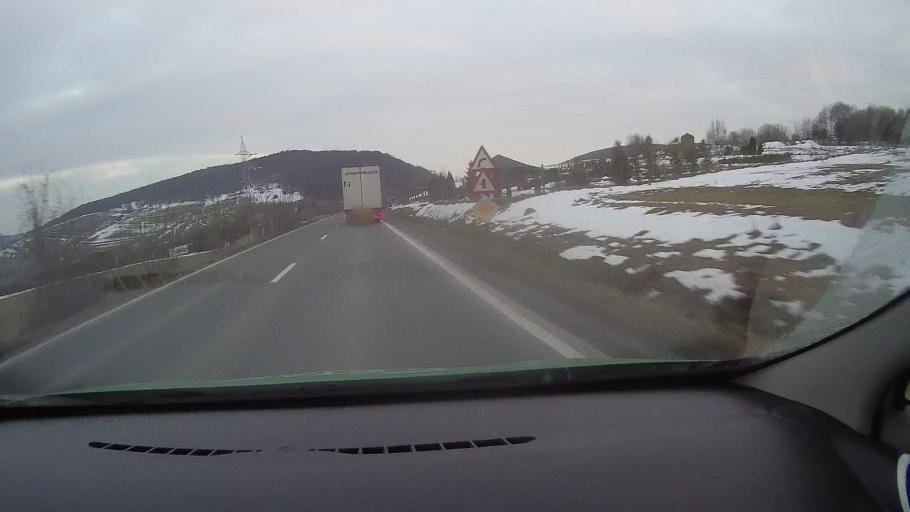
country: RO
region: Harghita
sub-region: Municipiul Odorheiu Secuiesc
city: Odorheiu Secuiesc
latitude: 46.3431
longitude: 25.2681
